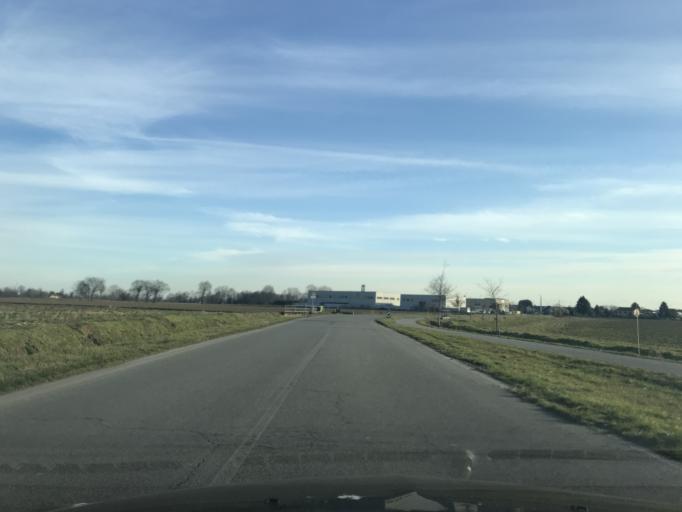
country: IT
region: Lombardy
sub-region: Provincia di Lodi
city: Bargano
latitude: 45.2460
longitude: 9.4403
